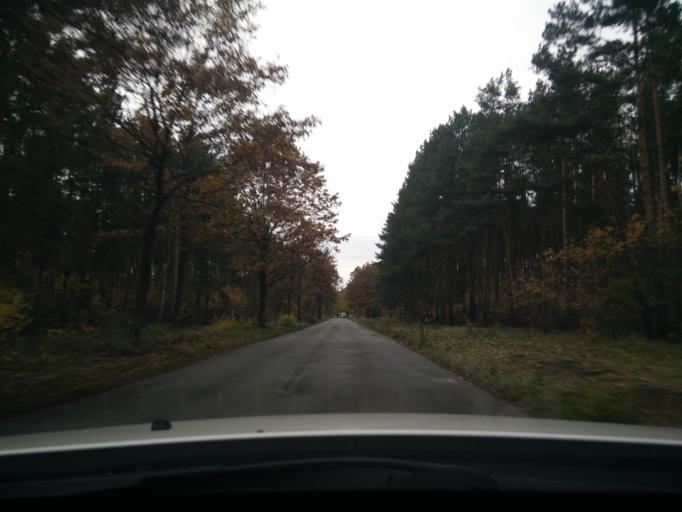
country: DE
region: Berlin
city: Staaken
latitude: 52.5677
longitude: 13.1333
